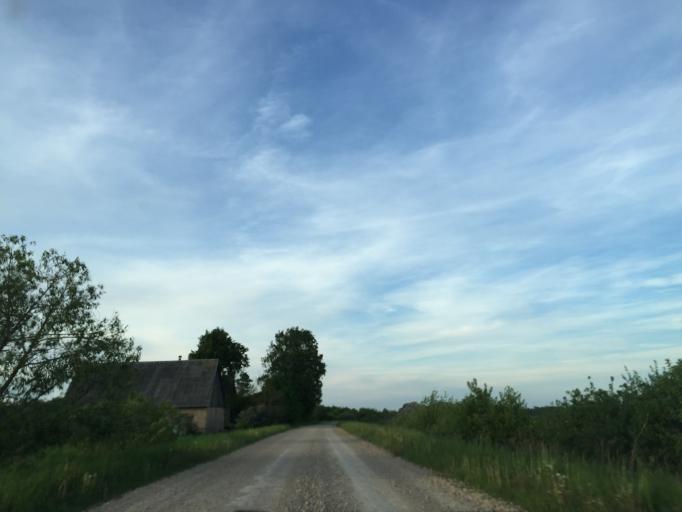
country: LV
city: Tireli
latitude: 56.7361
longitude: 23.5093
